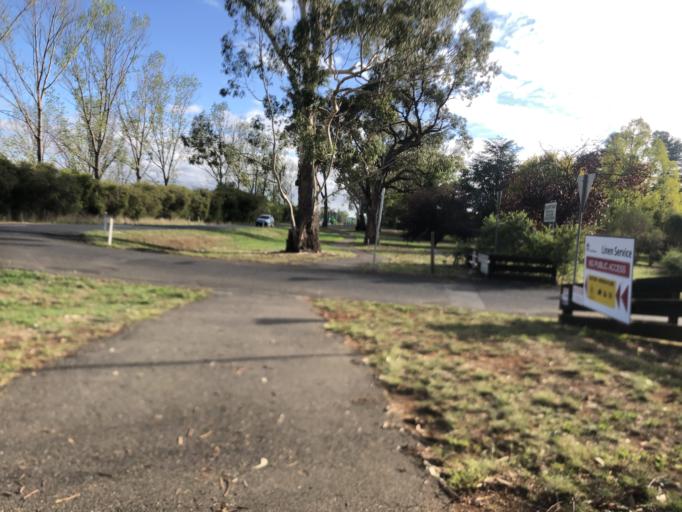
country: AU
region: New South Wales
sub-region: Orange Municipality
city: Orange
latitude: -33.3200
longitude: 149.0883
